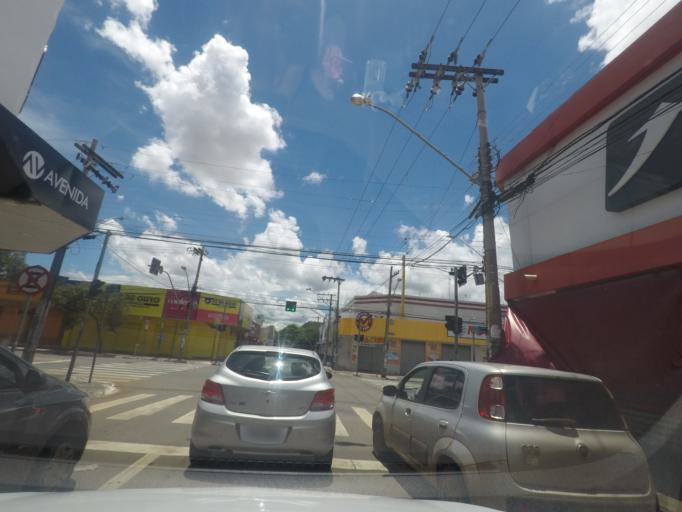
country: BR
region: Goias
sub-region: Goiania
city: Goiania
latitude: -16.6686
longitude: -49.2931
